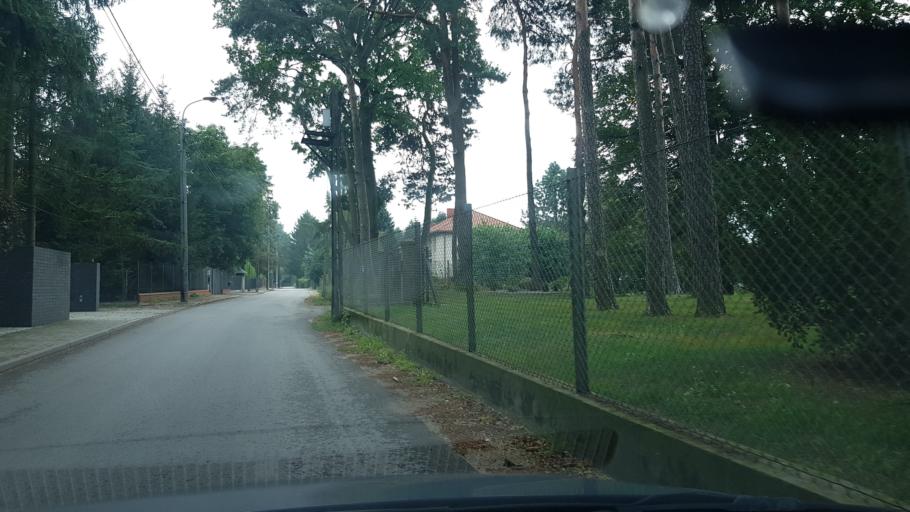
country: PL
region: Masovian Voivodeship
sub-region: Powiat piaseczynski
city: Konstancin-Jeziorna
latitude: 52.1034
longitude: 21.1046
